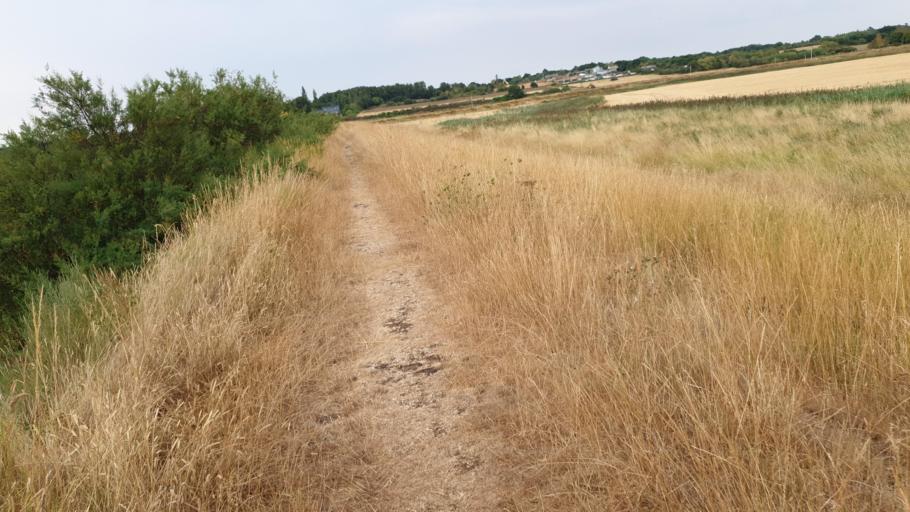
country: GB
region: England
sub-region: Essex
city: Alresford
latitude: 51.8342
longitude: 0.9878
